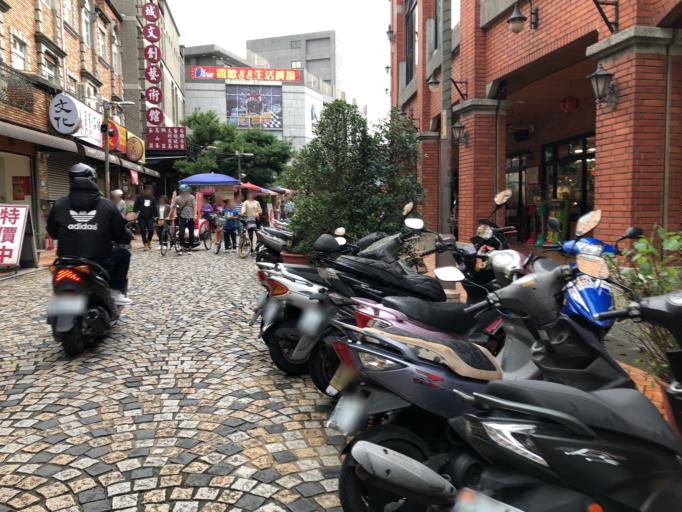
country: TW
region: Taiwan
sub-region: Taoyuan
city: Taoyuan
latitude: 24.9524
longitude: 121.3477
